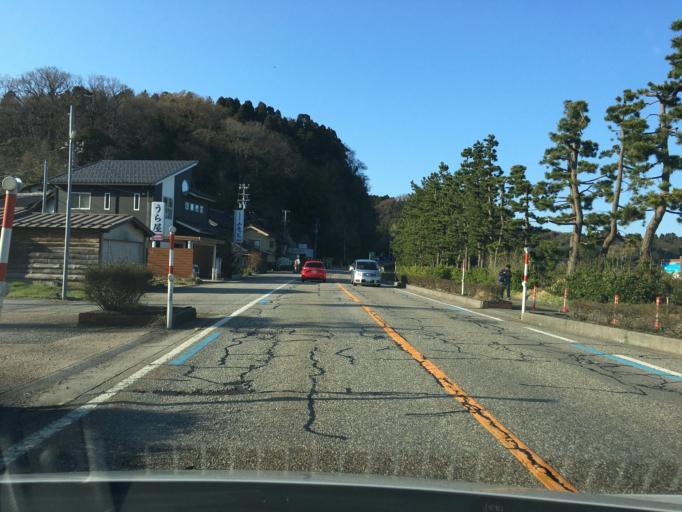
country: JP
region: Toyama
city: Himi
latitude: 36.9161
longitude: 137.0255
